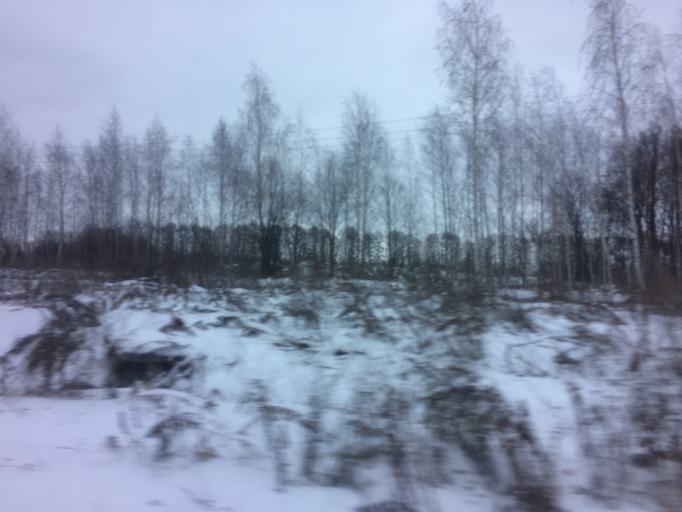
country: RU
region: Tula
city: Mendeleyevskiy
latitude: 54.1408
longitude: 37.6376
